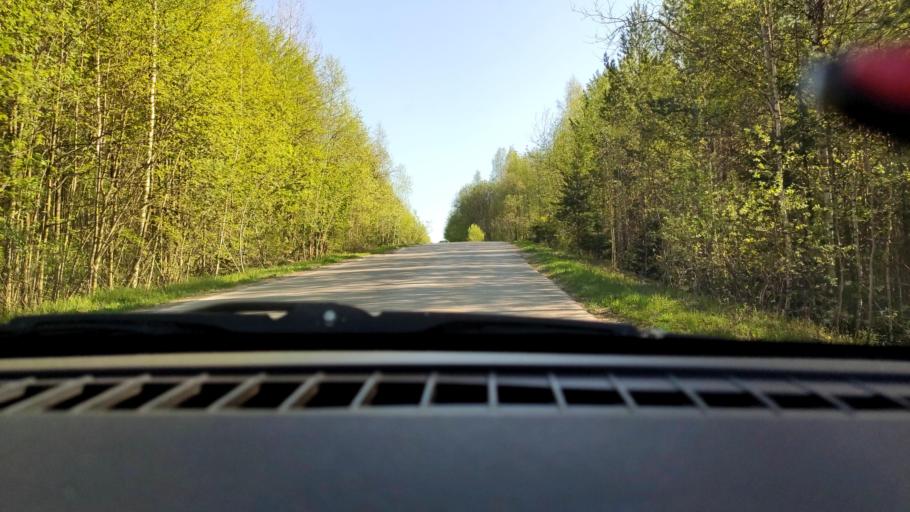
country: RU
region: Perm
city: Overyata
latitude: 58.0675
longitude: 56.0018
